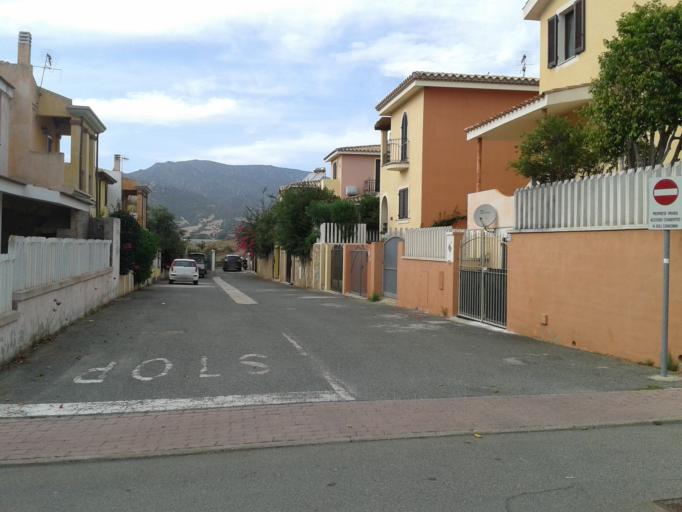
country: IT
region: Sardinia
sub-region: Provincia di Cagliari
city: Villasimius
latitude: 39.1511
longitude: 9.5193
